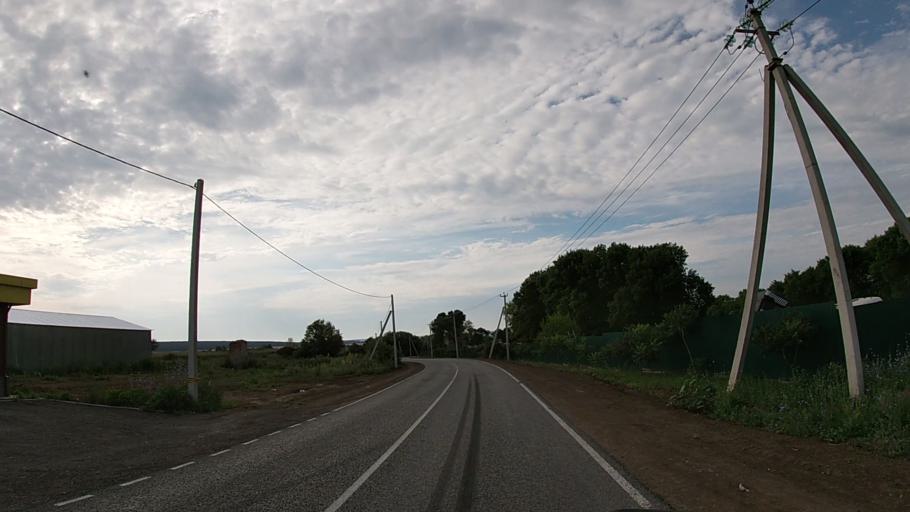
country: RU
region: Belgorod
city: Severnyy
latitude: 50.7195
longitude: 36.5862
